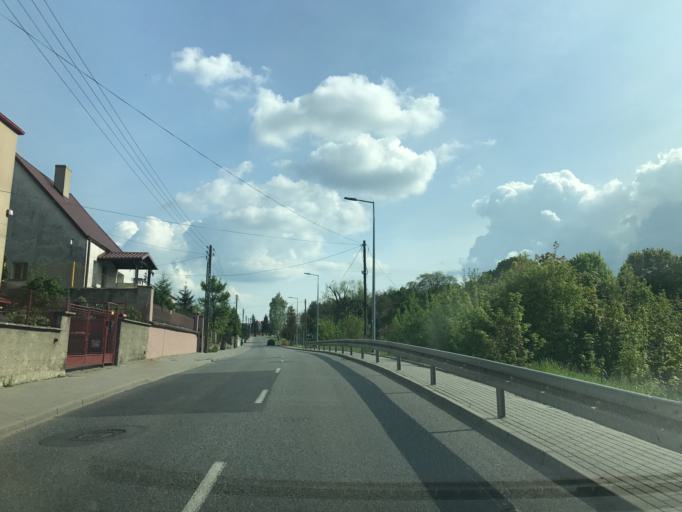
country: PL
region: Kujawsko-Pomorskie
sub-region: Bydgoszcz
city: Fordon
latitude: 53.1111
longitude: 18.1086
